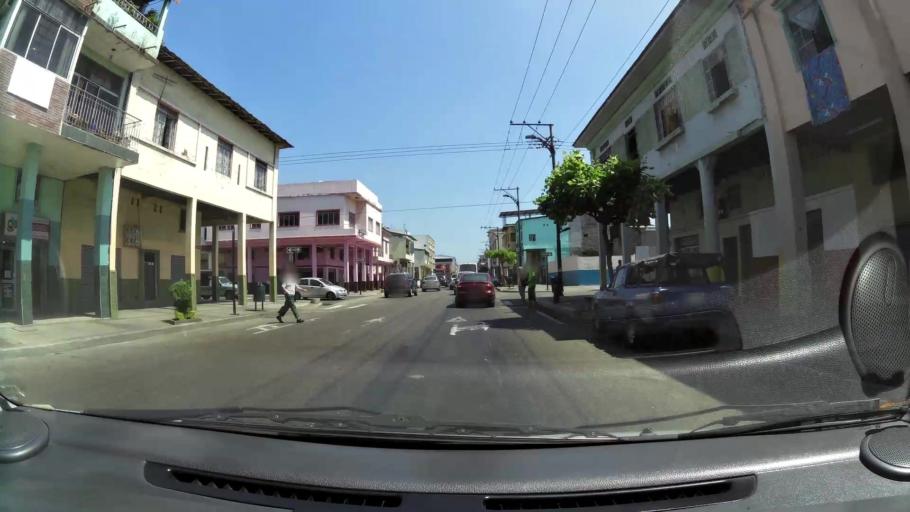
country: EC
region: Guayas
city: Guayaquil
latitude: -2.2051
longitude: -79.9037
